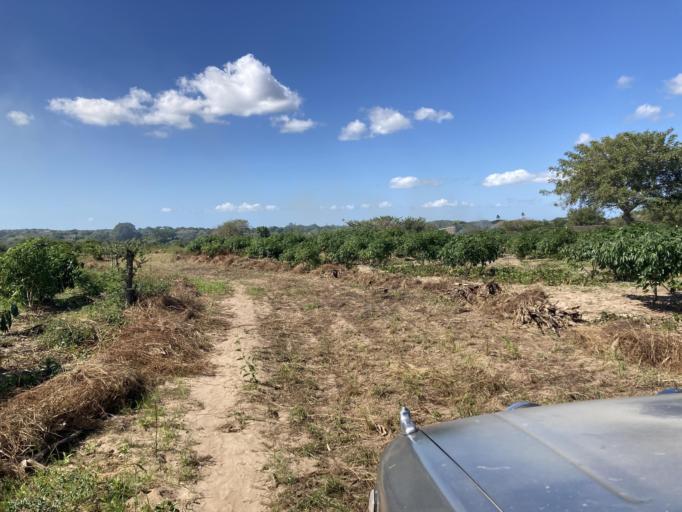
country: MZ
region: Maputo City
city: Maputo
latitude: -26.0505
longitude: 32.5506
